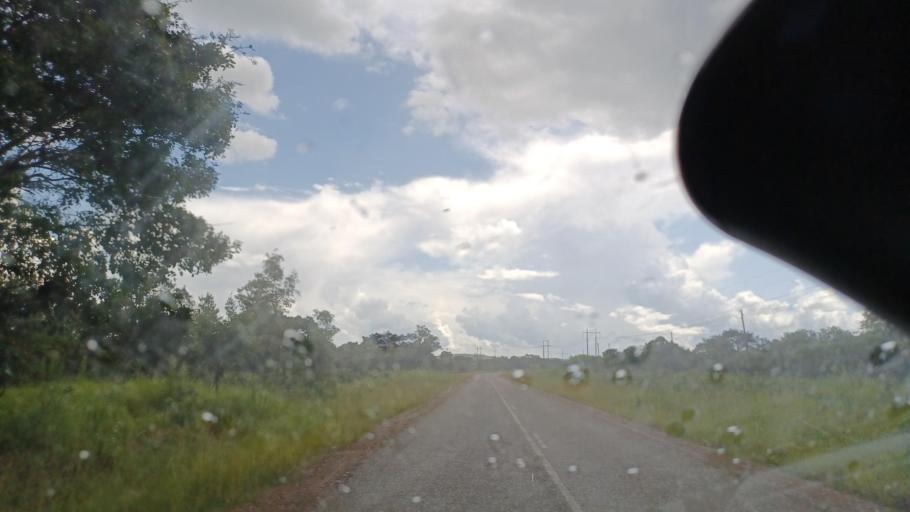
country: ZM
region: North-Western
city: Kasempa
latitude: -13.1040
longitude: 25.8836
